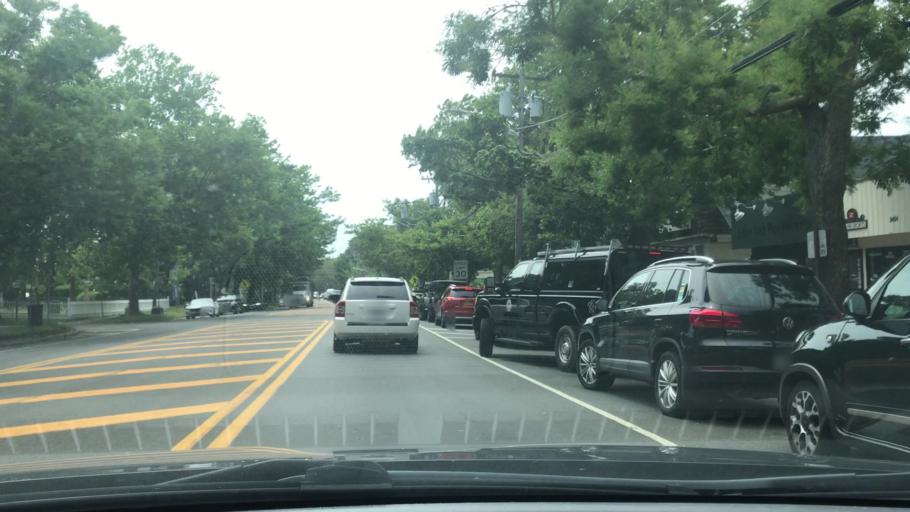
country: US
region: New York
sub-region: Suffolk County
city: Bridgehampton
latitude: 40.9370
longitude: -72.3025
